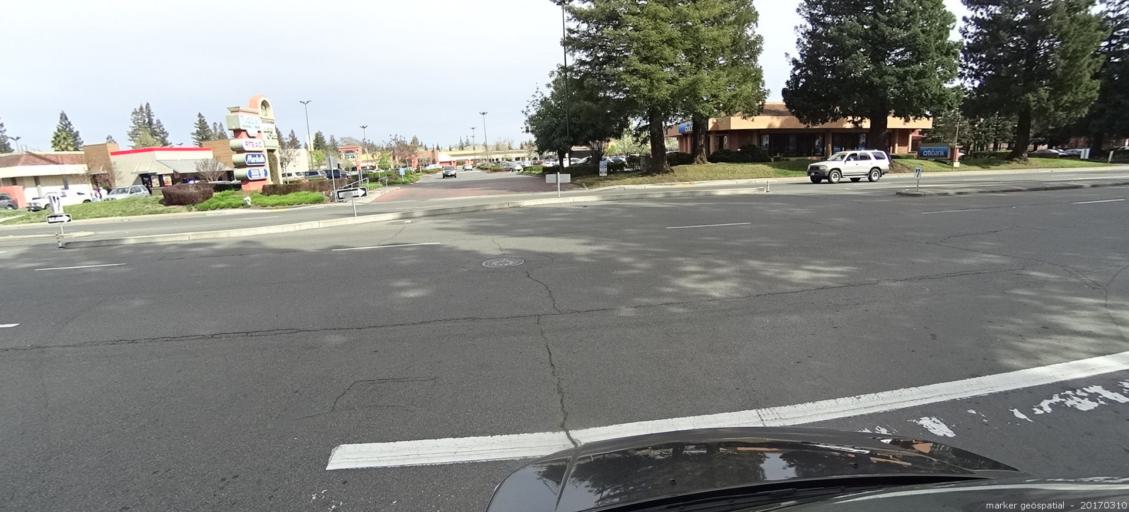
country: US
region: California
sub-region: Sacramento County
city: Parkway
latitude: 38.4944
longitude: -121.5242
